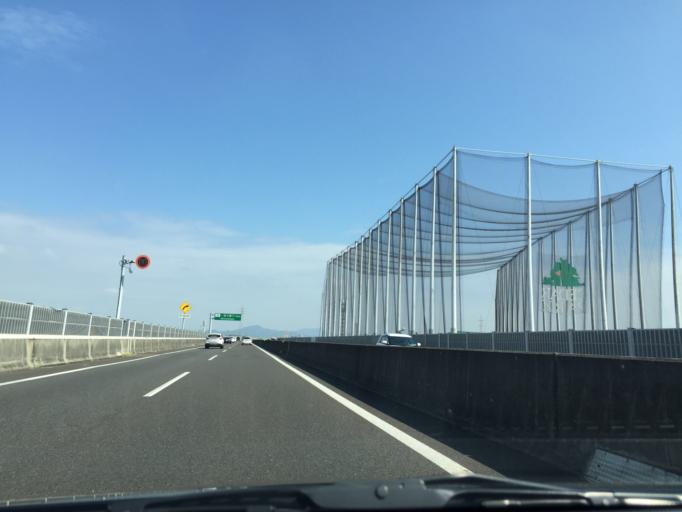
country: JP
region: Aichi
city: Kuroda
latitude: 35.3291
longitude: 136.7793
